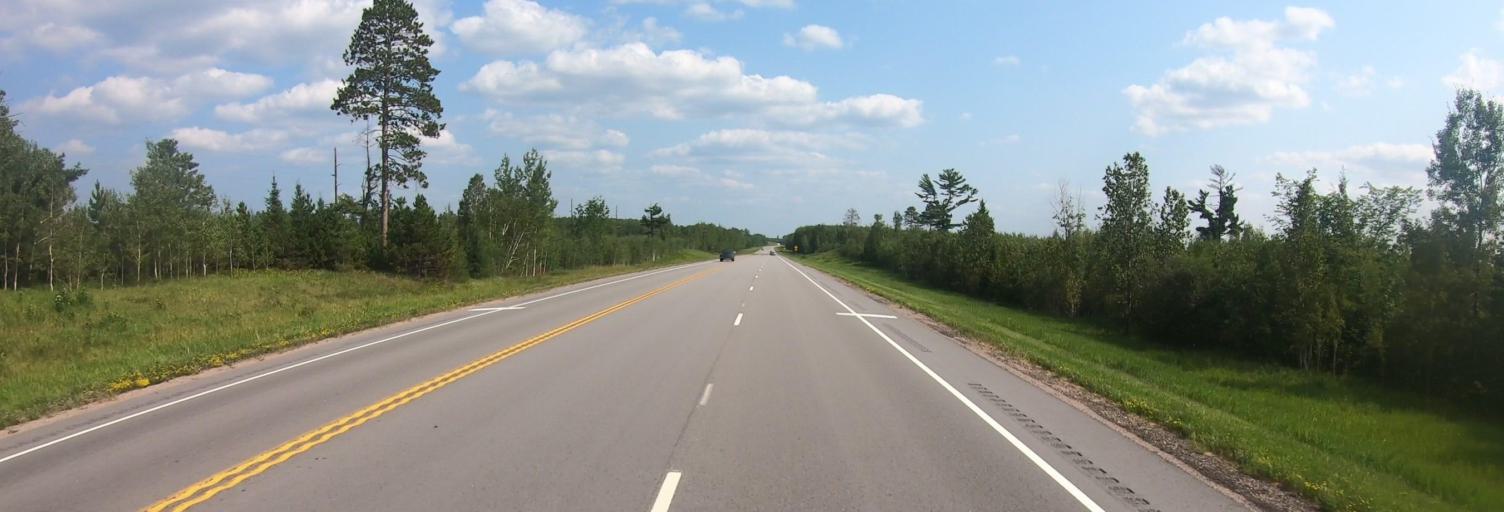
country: US
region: Minnesota
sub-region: Saint Louis County
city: Mountain Iron
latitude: 47.9025
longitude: -92.7899
